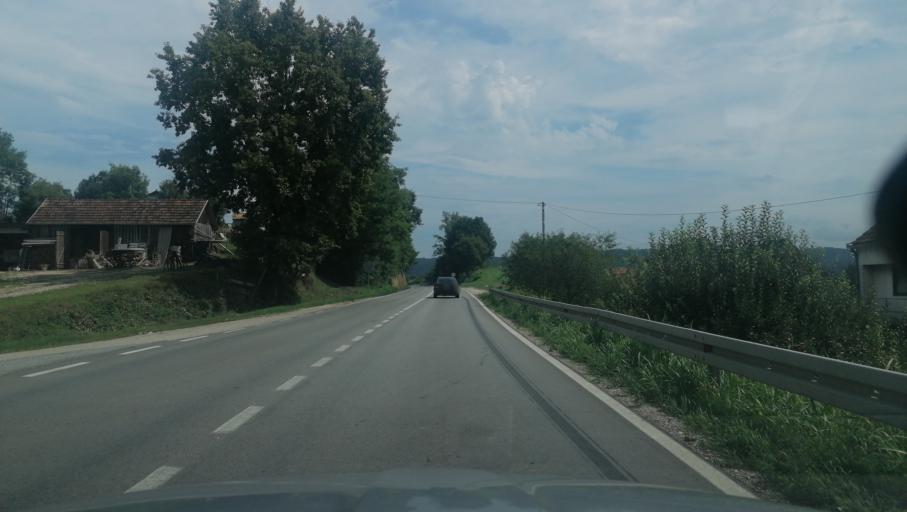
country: BA
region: Federation of Bosnia and Herzegovina
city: Odzak
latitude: 44.9325
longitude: 18.1935
